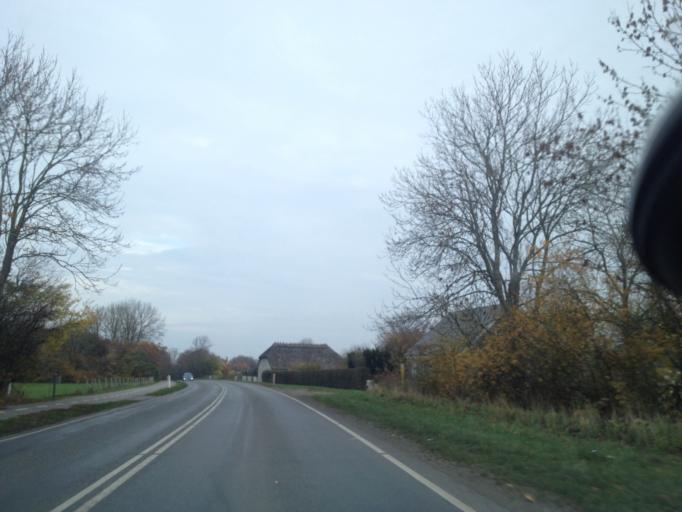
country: DK
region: South Denmark
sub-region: Nordfyns Kommune
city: Bogense
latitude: 55.5390
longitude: 10.0979
